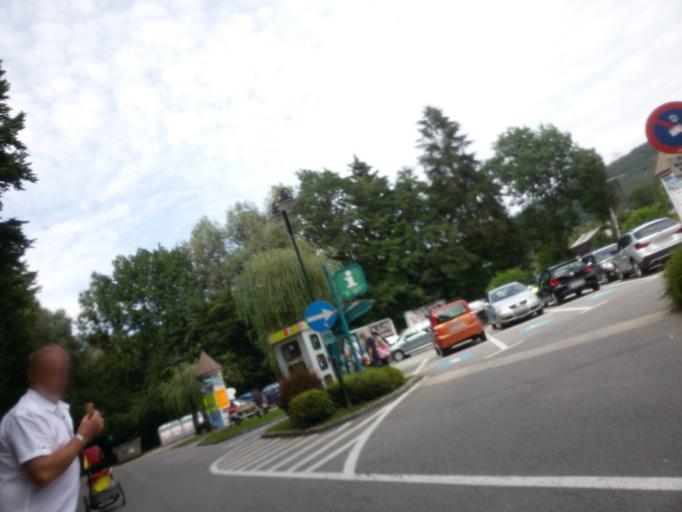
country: AT
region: Carinthia
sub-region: Politischer Bezirk Villach Land
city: Velden am Woerthersee
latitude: 46.6175
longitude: 14.0476
